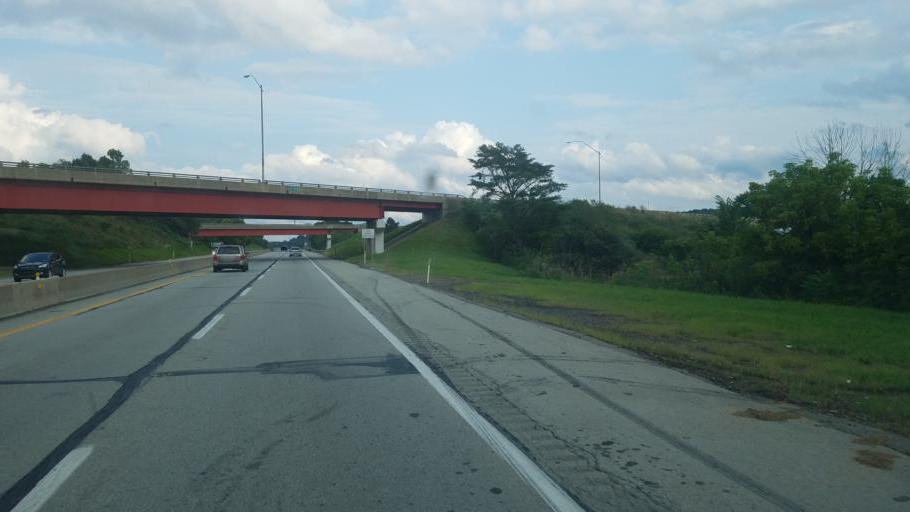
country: US
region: Pennsylvania
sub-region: Allegheny County
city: Bradford Woods
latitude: 40.6619
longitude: -80.0931
